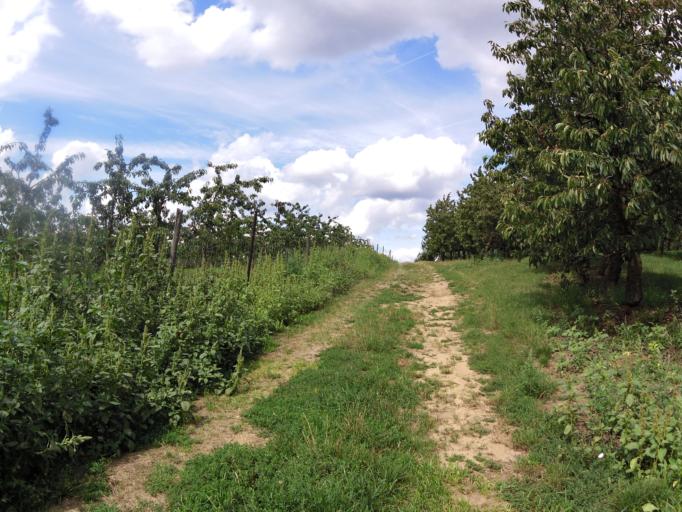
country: DE
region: Bavaria
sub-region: Regierungsbezirk Unterfranken
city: Sommerhausen
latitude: 49.7061
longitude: 10.0359
